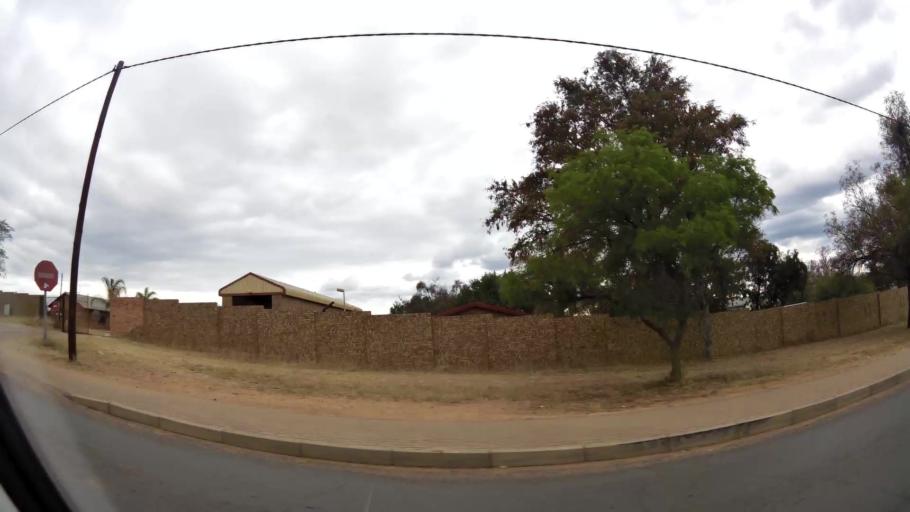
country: ZA
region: Limpopo
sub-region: Waterberg District Municipality
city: Modimolle
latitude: -24.7000
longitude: 28.4162
